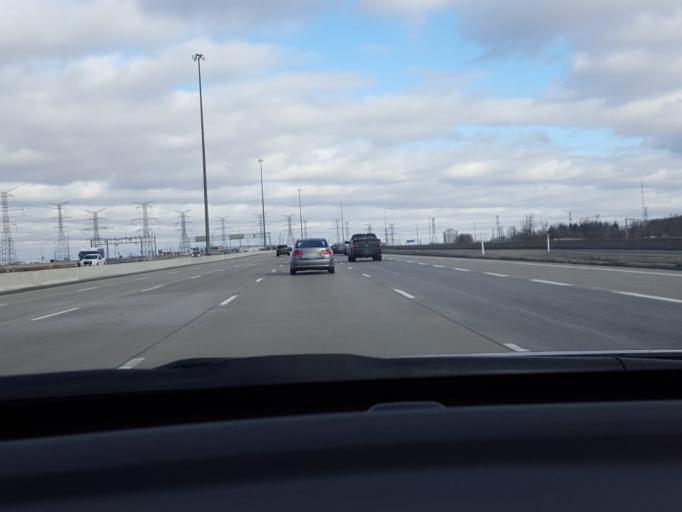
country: CA
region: Ontario
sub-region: York
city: Richmond Hill
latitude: 43.8349
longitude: -79.4268
